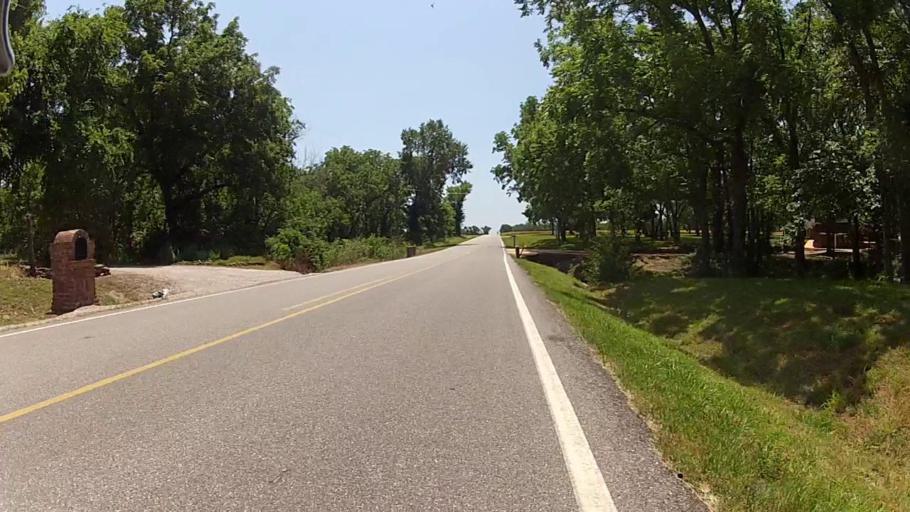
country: US
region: Kansas
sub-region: Montgomery County
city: Cherryvale
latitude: 37.2463
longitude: -95.5373
